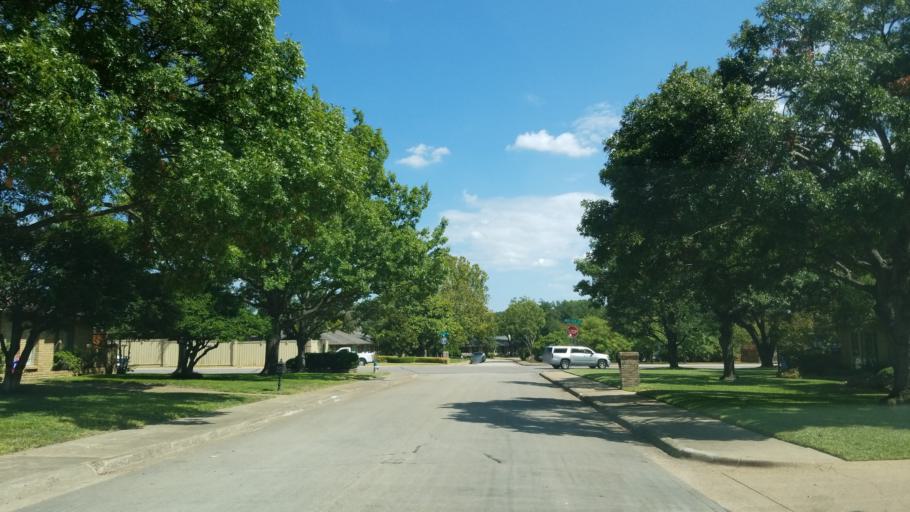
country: US
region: Texas
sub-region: Dallas County
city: Addison
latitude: 32.9537
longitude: -96.7874
